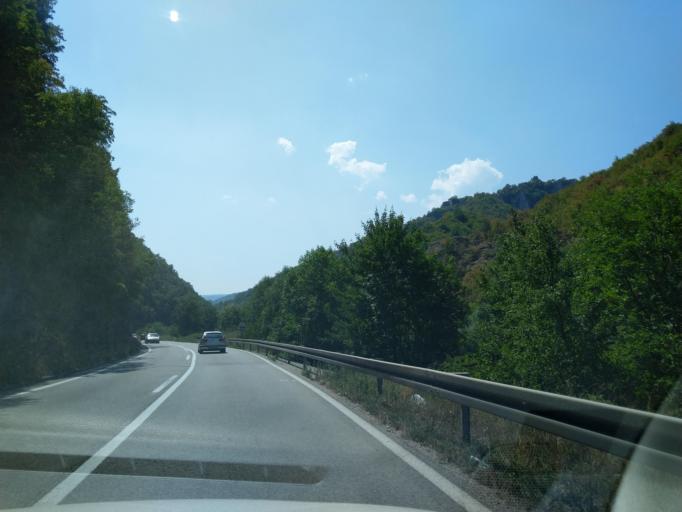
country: RS
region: Central Serbia
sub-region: Zlatiborski Okrug
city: Prijepolje
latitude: 43.4593
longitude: 19.6458
